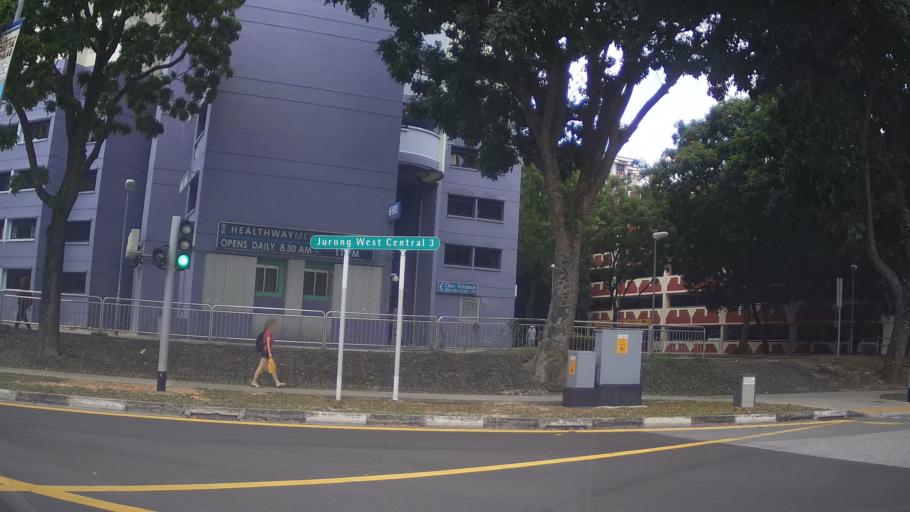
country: MY
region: Johor
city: Johor Bahru
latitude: 1.3398
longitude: 103.7070
